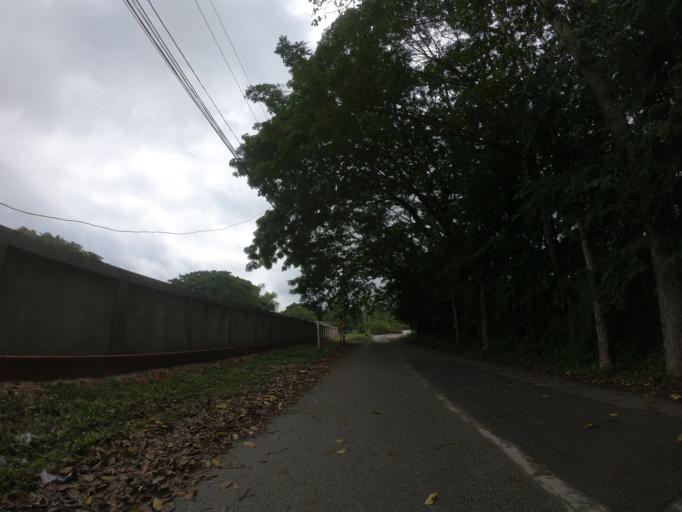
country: TH
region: Chiang Mai
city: San Sai
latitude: 18.8428
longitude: 99.0075
